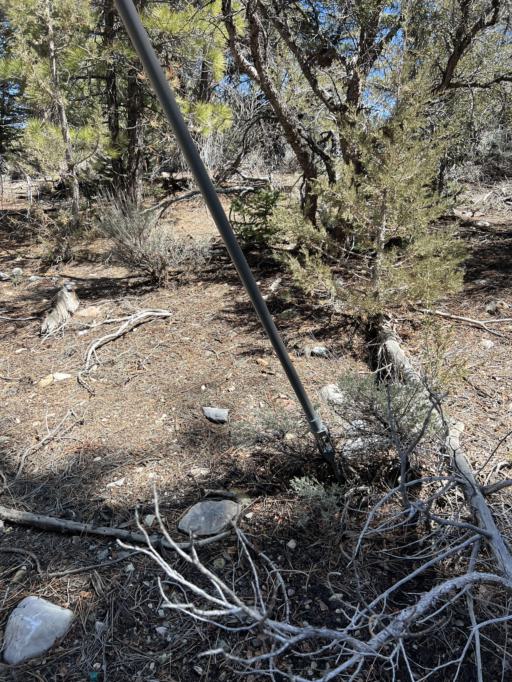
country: US
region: California
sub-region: San Bernardino County
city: Big Bear Lake
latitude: 34.3245
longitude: -116.9328
